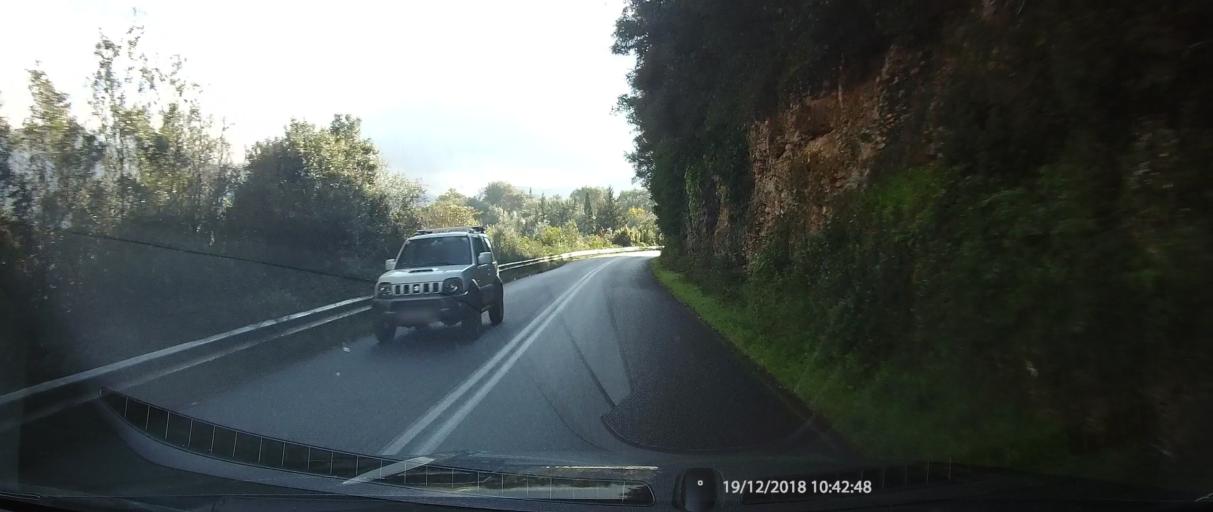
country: GR
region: Peloponnese
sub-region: Nomos Messinias
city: Paralia Vergas
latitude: 36.9529
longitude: 22.1929
